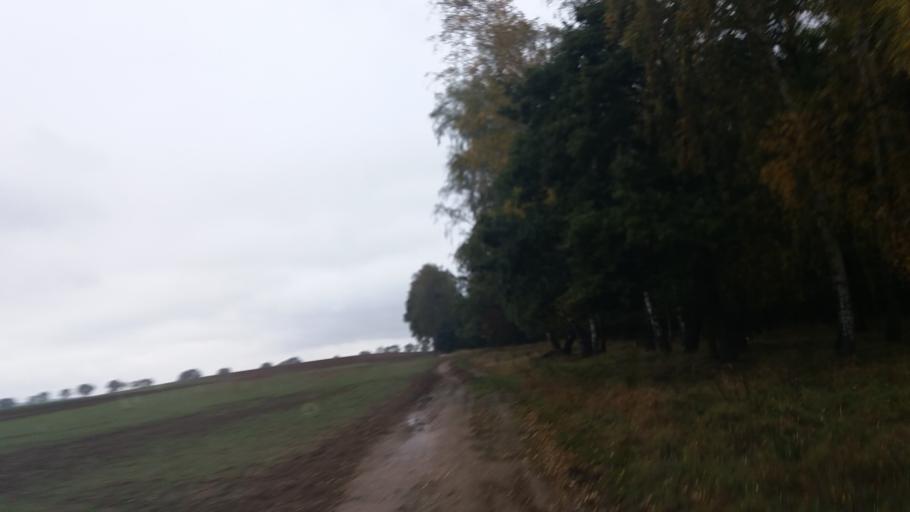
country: PL
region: West Pomeranian Voivodeship
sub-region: Powiat choszczenski
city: Pelczyce
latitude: 53.0707
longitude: 15.2722
